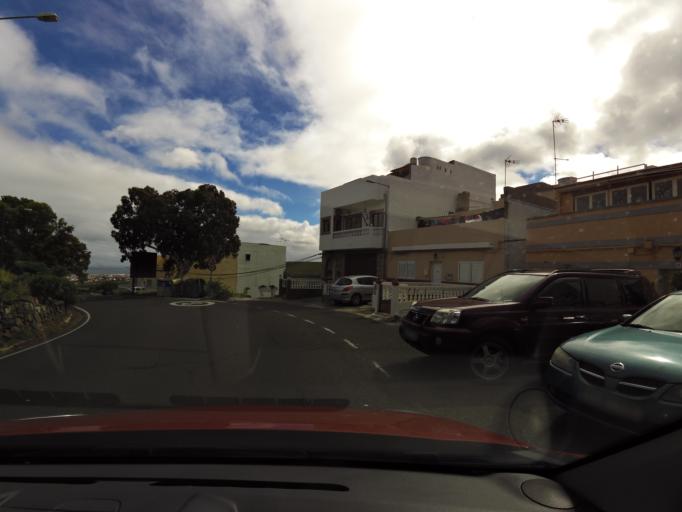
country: ES
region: Canary Islands
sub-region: Provincia de Las Palmas
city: Telde
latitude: 28.0116
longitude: -15.4398
